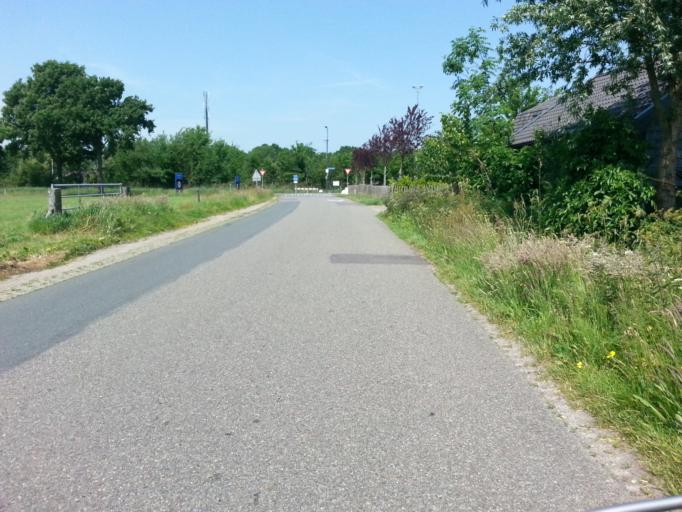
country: NL
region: Gelderland
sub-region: Gemeente Barneveld
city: Terschuur
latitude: 52.1337
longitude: 5.5121
